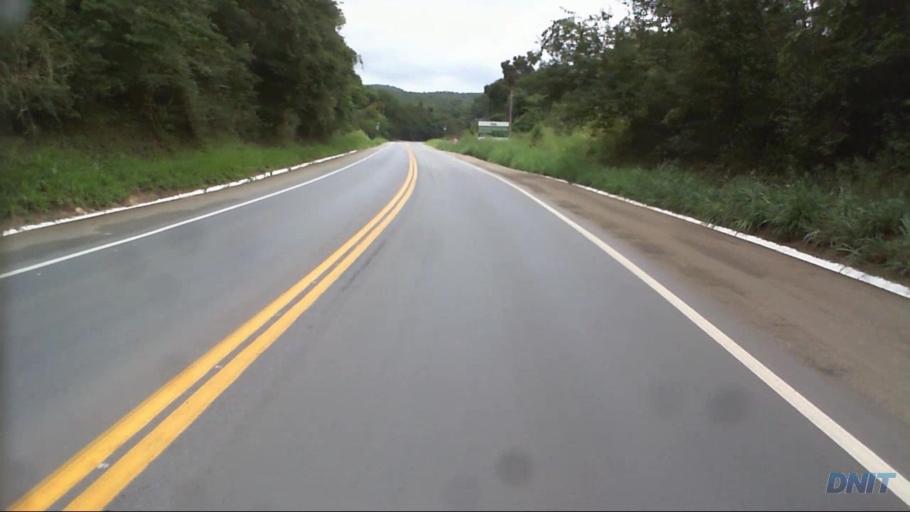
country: BR
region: Minas Gerais
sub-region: Barao De Cocais
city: Barao de Cocais
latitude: -19.8045
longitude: -43.4036
